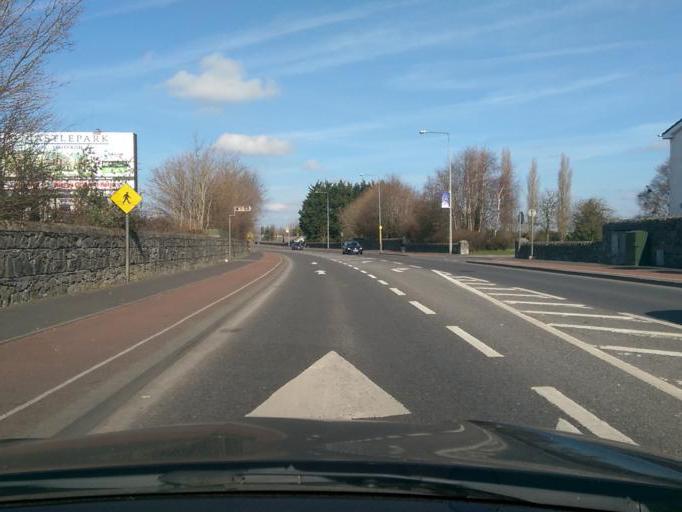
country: IE
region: Leinster
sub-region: Kildare
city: Maynooth
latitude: 53.3758
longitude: -6.5878
